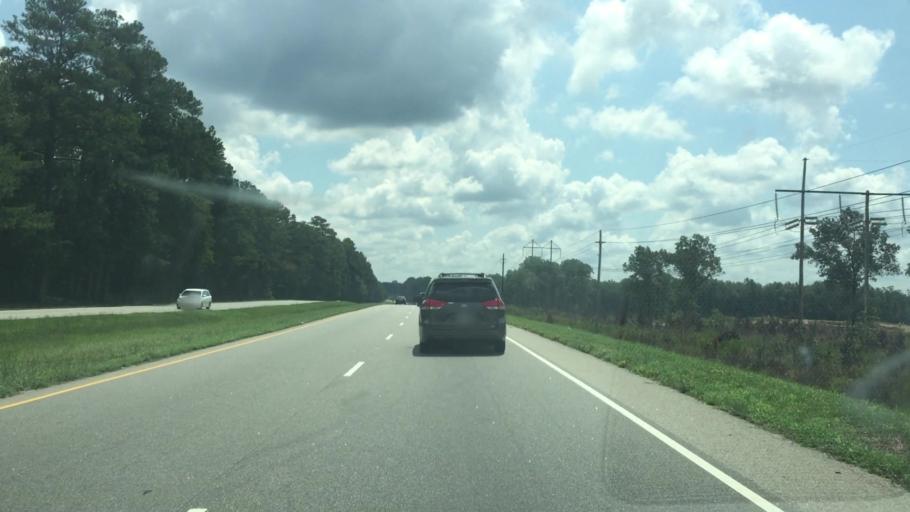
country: US
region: North Carolina
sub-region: Scotland County
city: Laurel Hill
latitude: 34.8173
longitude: -79.5734
